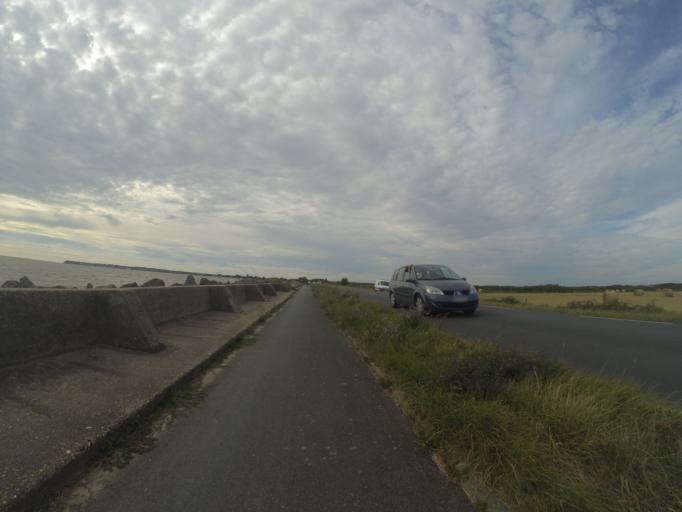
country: FR
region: Poitou-Charentes
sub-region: Departement de la Charente-Maritime
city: Meschers-sur-Gironde
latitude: 45.5442
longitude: -0.9103
